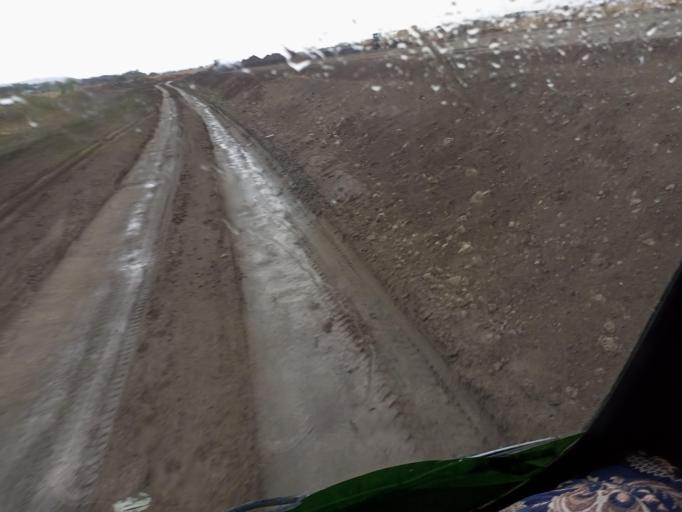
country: ET
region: Oromiya
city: Ziway
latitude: 7.7588
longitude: 38.6105
